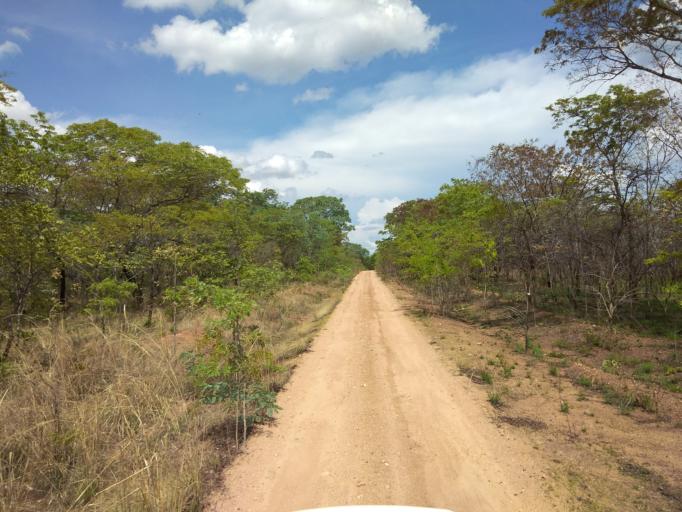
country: ZM
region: Central
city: Mkushi
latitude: -14.1334
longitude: 30.0522
